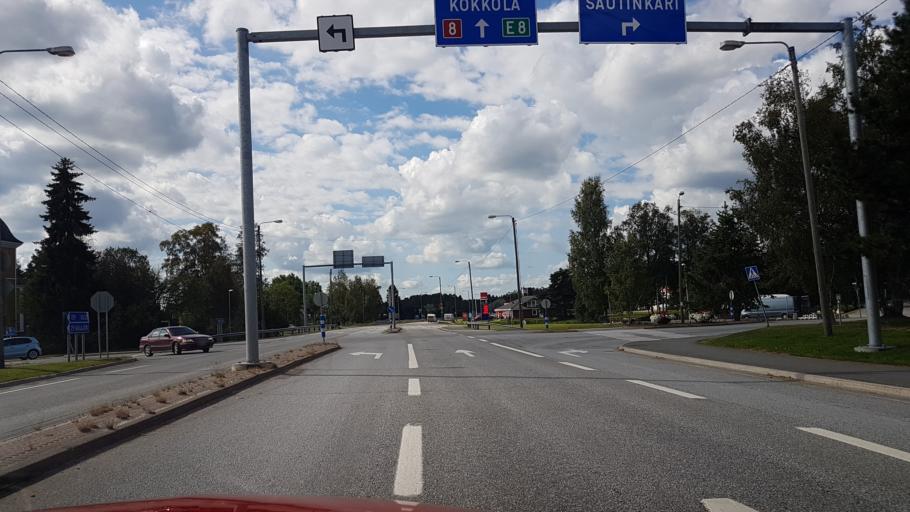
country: FI
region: Northern Ostrobothnia
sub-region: Ylivieska
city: Himanka
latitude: 64.0619
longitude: 23.6549
